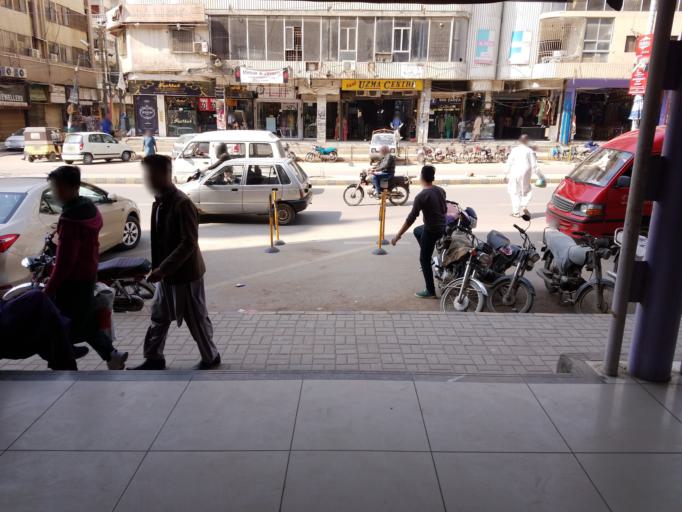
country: PK
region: Sindh
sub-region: Karachi District
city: Karachi
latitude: 24.8737
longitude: 67.0612
